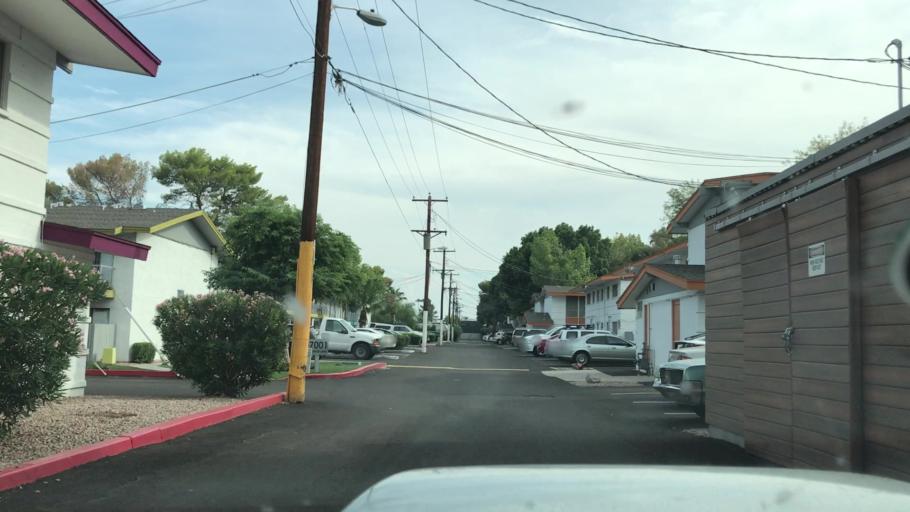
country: US
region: Arizona
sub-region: Maricopa County
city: Scottsdale
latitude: 33.4692
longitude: -111.9300
